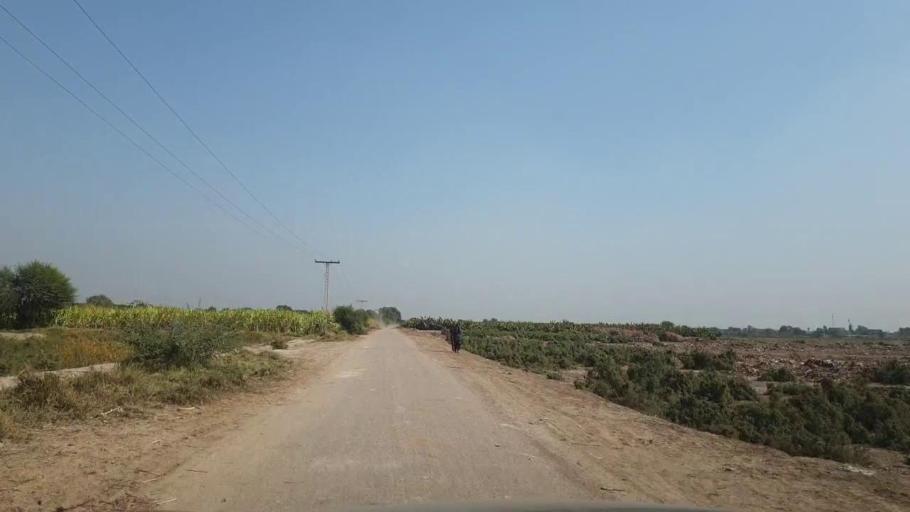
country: PK
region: Sindh
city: Tando Allahyar
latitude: 25.5558
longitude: 68.7043
